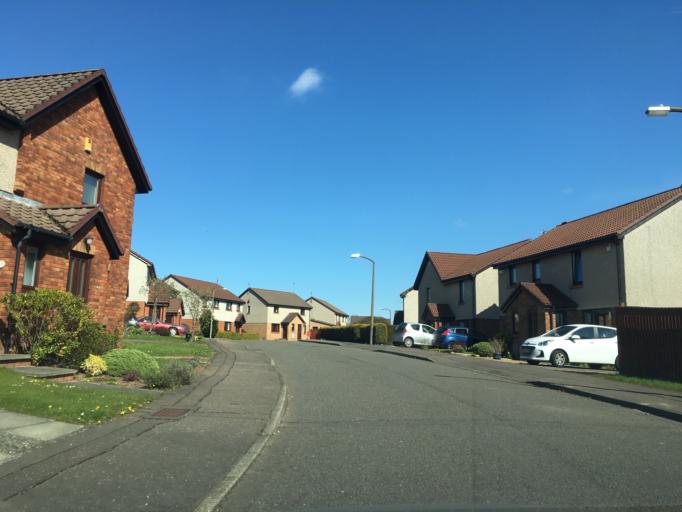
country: GB
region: Scotland
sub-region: Edinburgh
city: Colinton
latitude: 55.9004
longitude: -3.2292
